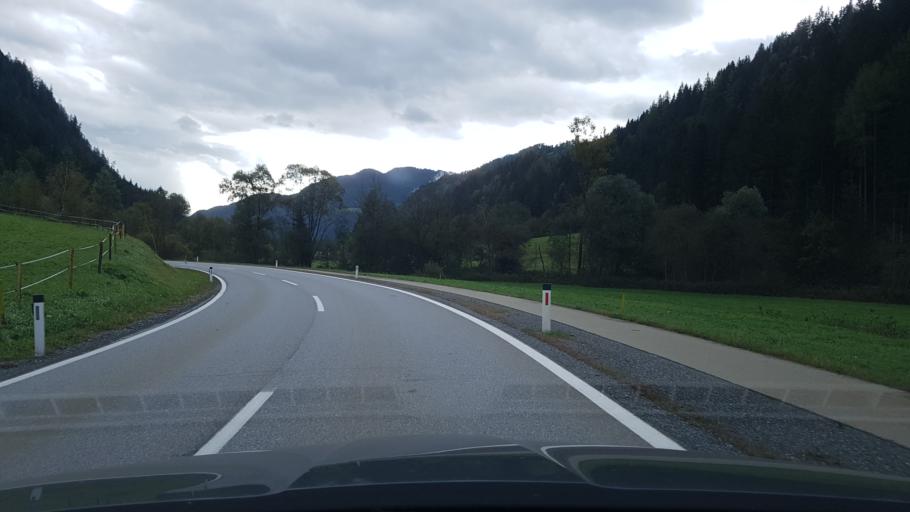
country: AT
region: Styria
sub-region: Politischer Bezirk Murau
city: Oberwolz Stadt
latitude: 47.1584
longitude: 14.2552
